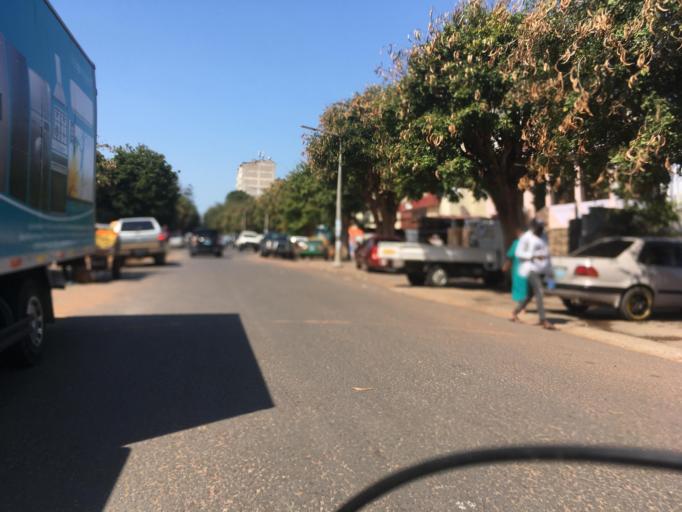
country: MZ
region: Maputo City
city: Maputo
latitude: -25.9650
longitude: 32.5751
